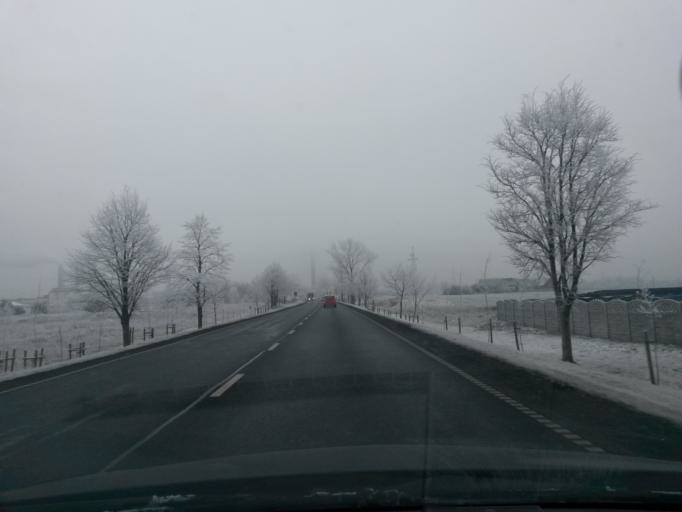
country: PL
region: Greater Poland Voivodeship
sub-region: Powiat gnieznienski
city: Trzemeszno
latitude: 52.5620
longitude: 17.8005
